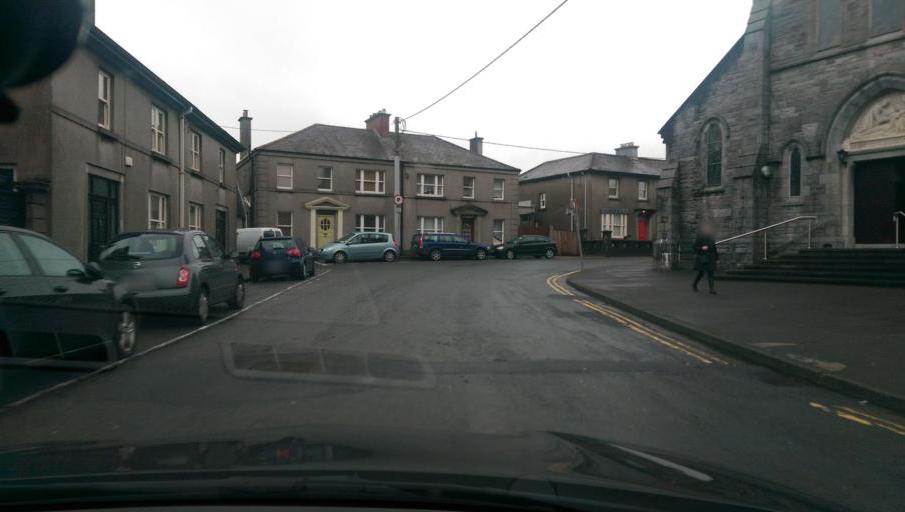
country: IE
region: Connaught
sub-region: County Galway
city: Gaillimh
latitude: 53.2731
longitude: -9.0601
